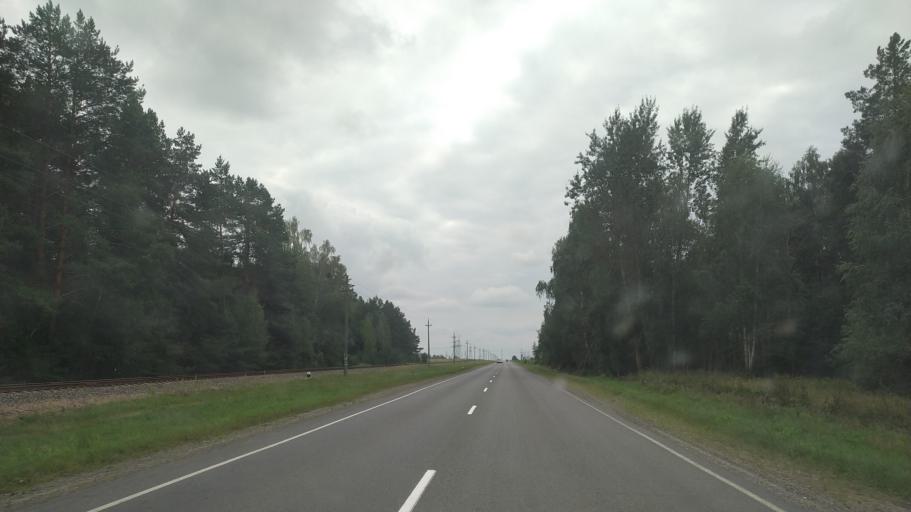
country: BY
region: Brest
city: Byelaazyorsk
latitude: 52.5242
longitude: 25.1483
